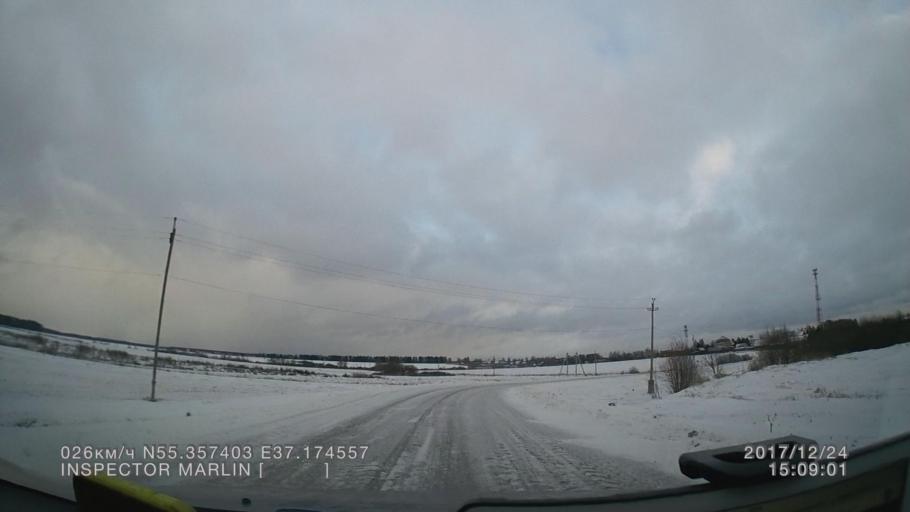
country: RU
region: Moskovskaya
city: Troitsk
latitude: 55.3579
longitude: 37.1743
